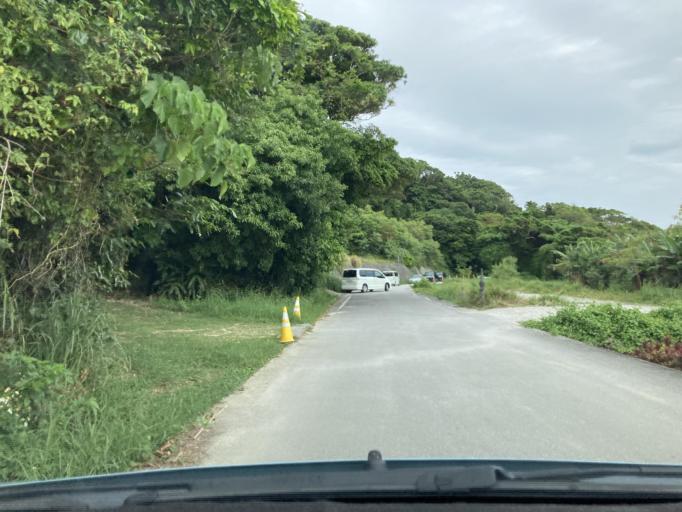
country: JP
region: Okinawa
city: Tomigusuku
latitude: 26.1393
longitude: 127.7953
